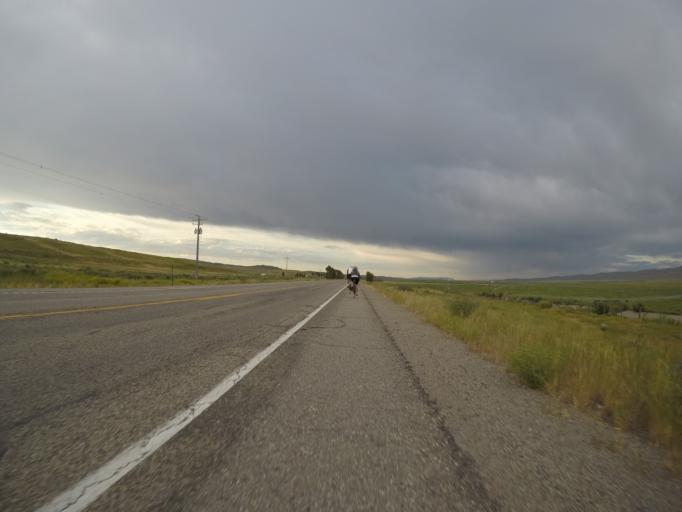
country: US
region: Utah
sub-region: Rich County
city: Randolph
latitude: 42.0461
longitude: -110.9314
